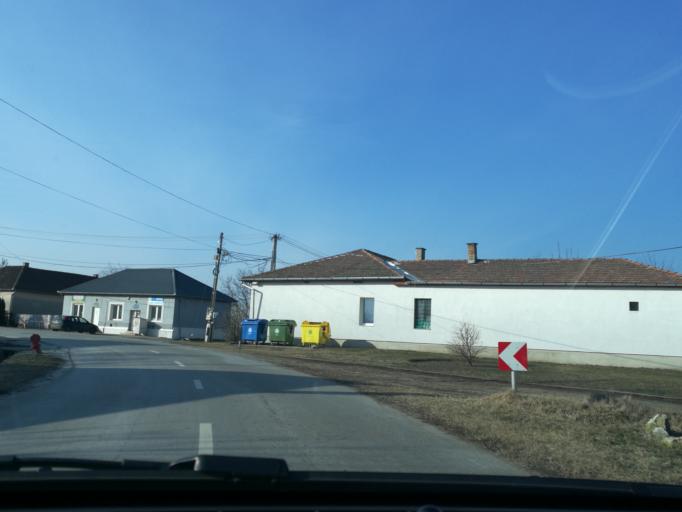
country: HU
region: Szabolcs-Szatmar-Bereg
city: Apagy
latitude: 48.0252
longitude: 21.9606
